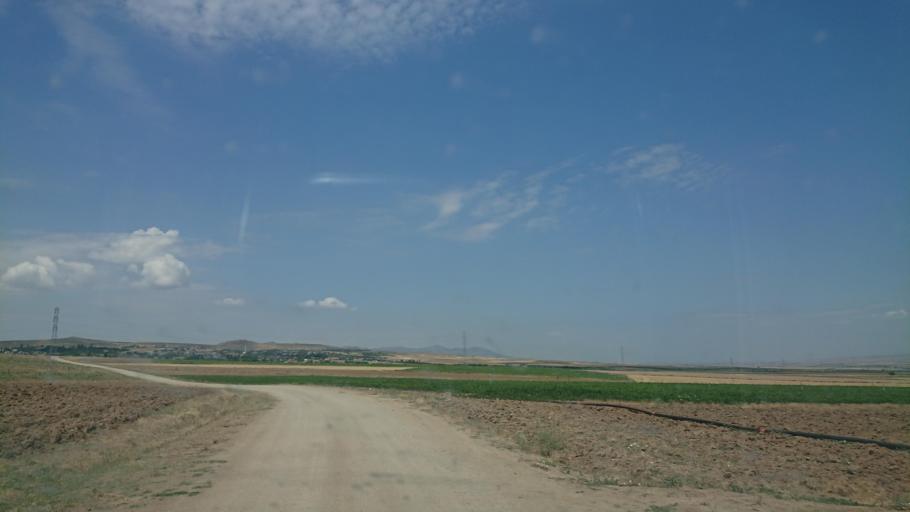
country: TR
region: Aksaray
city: Sariyahsi
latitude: 38.9575
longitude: 33.9110
